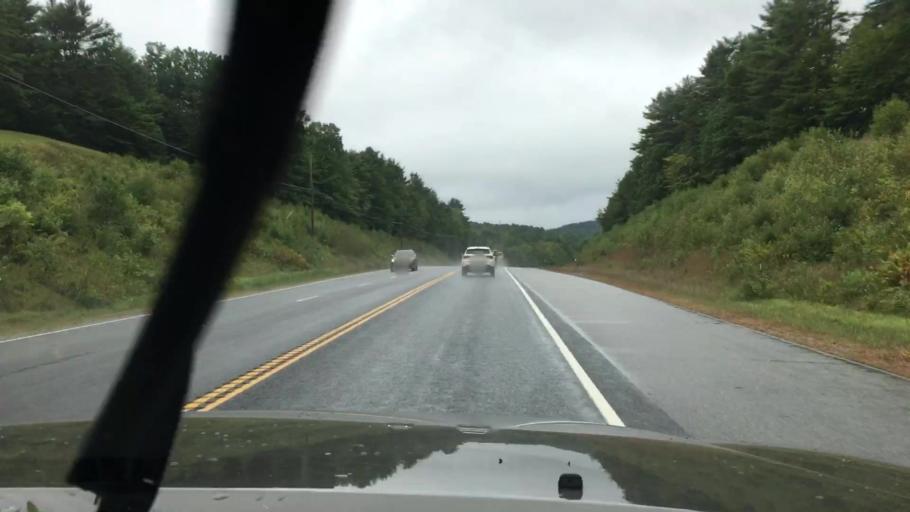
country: US
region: New Hampshire
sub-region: Cheshire County
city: Harrisville
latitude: 43.0008
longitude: -72.1798
